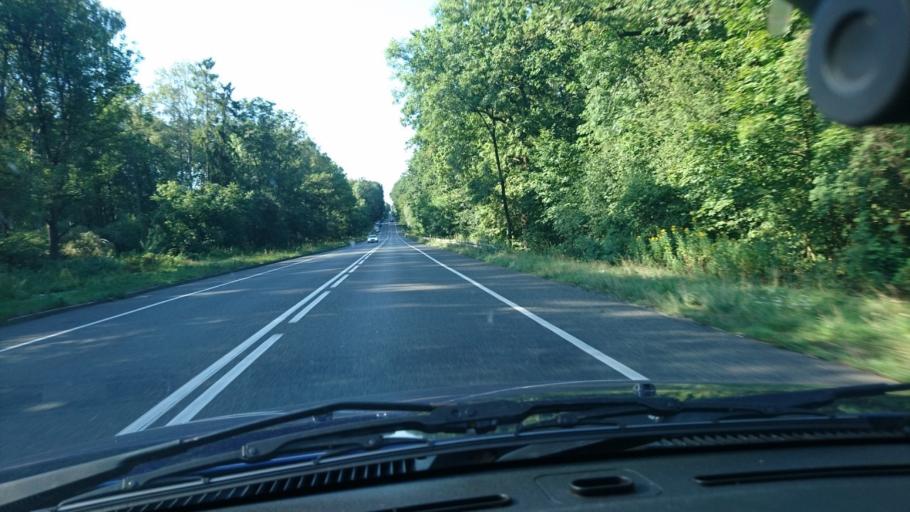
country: PL
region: Silesian Voivodeship
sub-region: Gliwice
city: Gliwice
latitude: 50.3273
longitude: 18.6601
